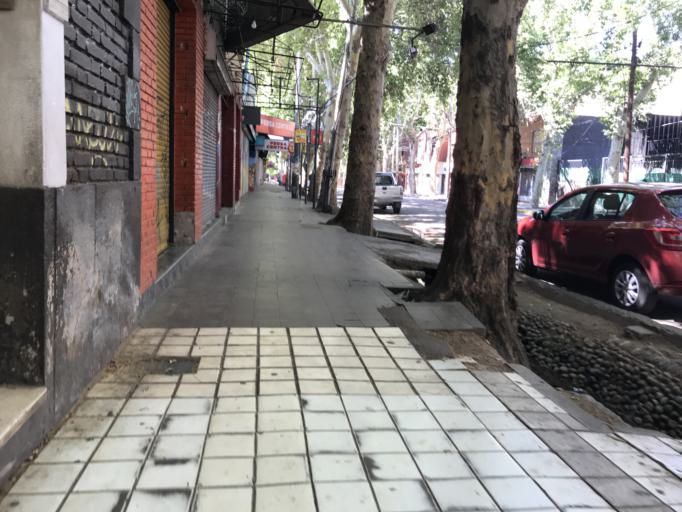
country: AR
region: Mendoza
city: Mendoza
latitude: -32.8847
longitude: -68.8405
